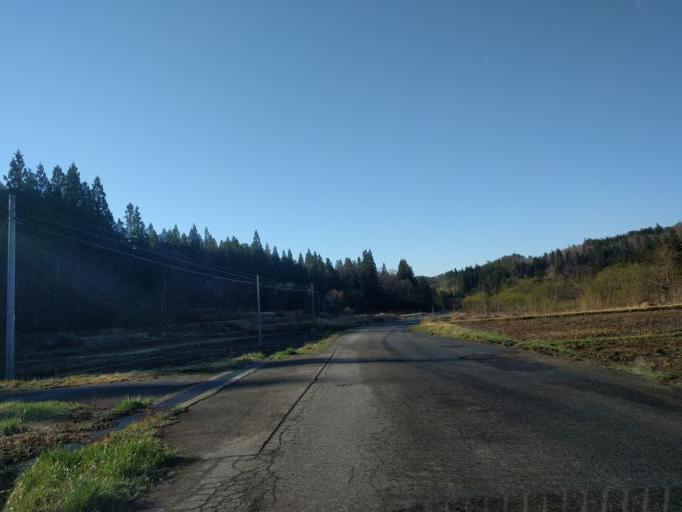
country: JP
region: Fukushima
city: Kitakata
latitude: 37.7111
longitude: 139.7834
